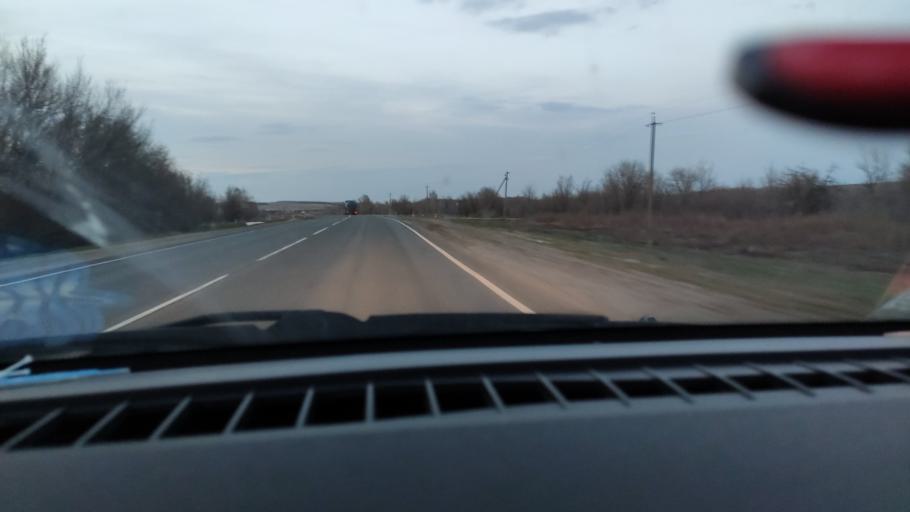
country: RU
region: Saratov
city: Sinodskoye
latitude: 52.0365
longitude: 46.7291
